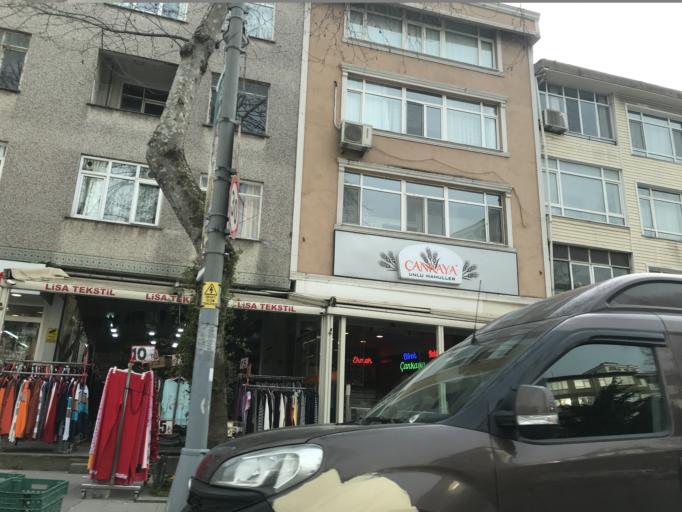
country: TR
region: Istanbul
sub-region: Atasehir
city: Atasehir
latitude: 40.9617
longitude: 29.0925
